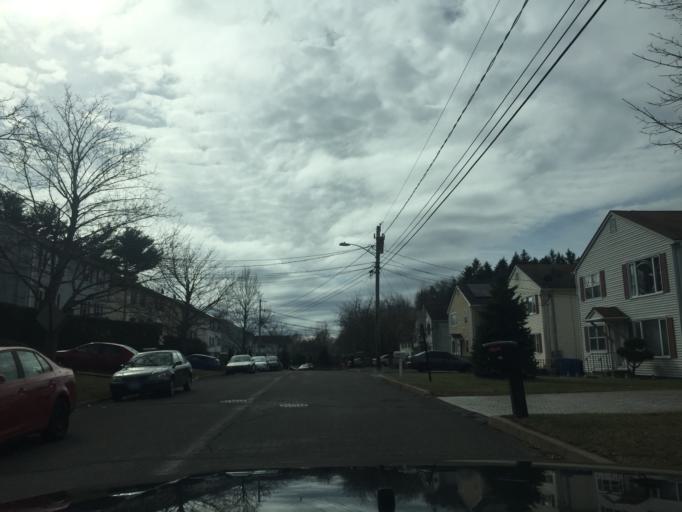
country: US
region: Connecticut
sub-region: Hartford County
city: New Britain
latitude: 41.6916
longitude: -72.7873
